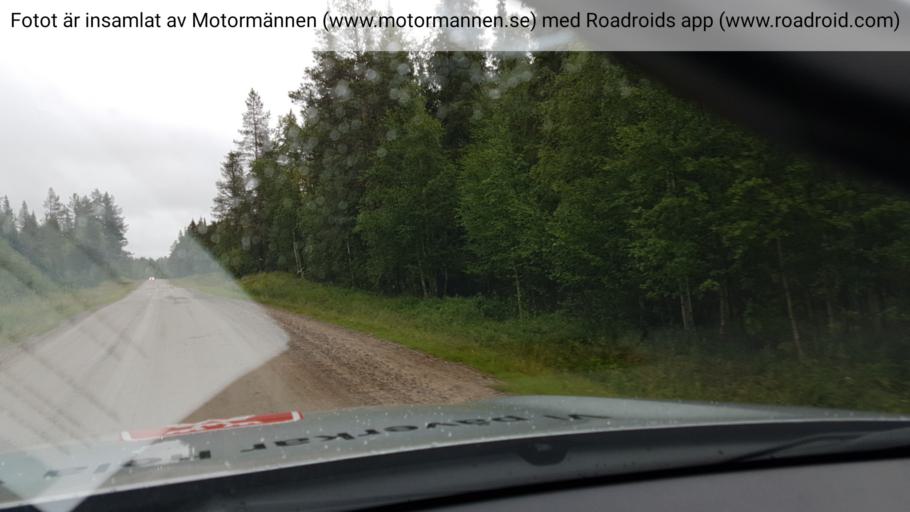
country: SE
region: Norrbotten
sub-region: Gallivare Kommun
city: Gaellivare
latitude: 66.7006
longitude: 20.4197
